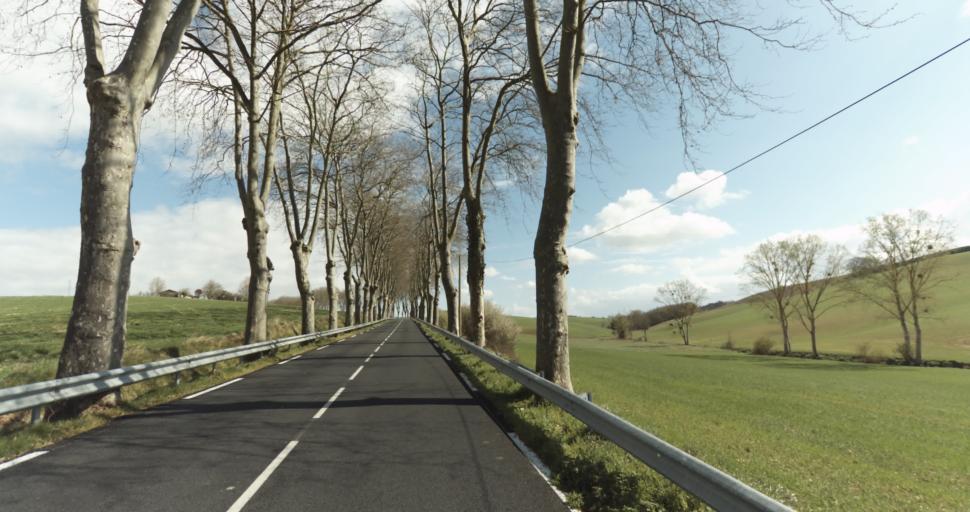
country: FR
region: Midi-Pyrenees
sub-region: Departement de la Haute-Garonne
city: Auterive
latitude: 43.3567
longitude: 1.5077
